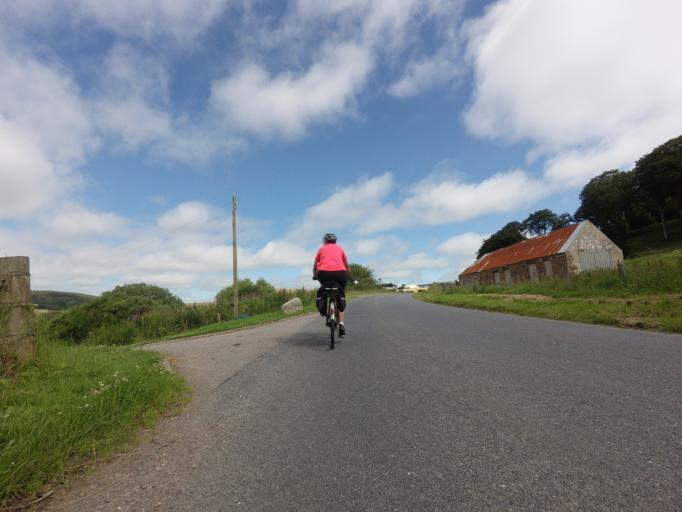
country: GB
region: Scotland
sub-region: Aberdeenshire
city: Turriff
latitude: 57.5632
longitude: -2.4941
